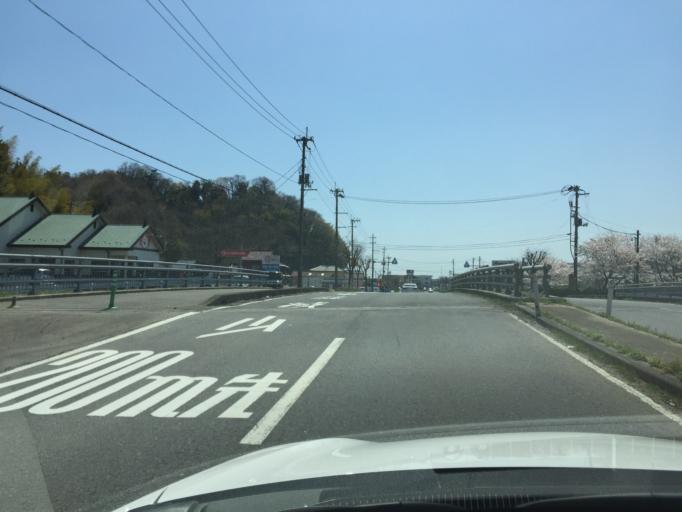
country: JP
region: Fukushima
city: Iwaki
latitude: 36.9857
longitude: 140.8712
